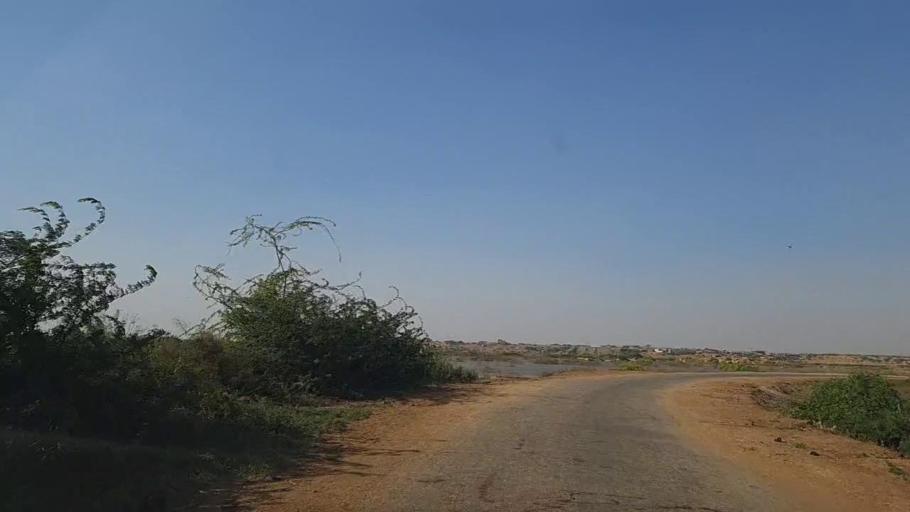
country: PK
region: Sindh
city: Daro Mehar
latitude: 24.9876
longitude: 68.1319
